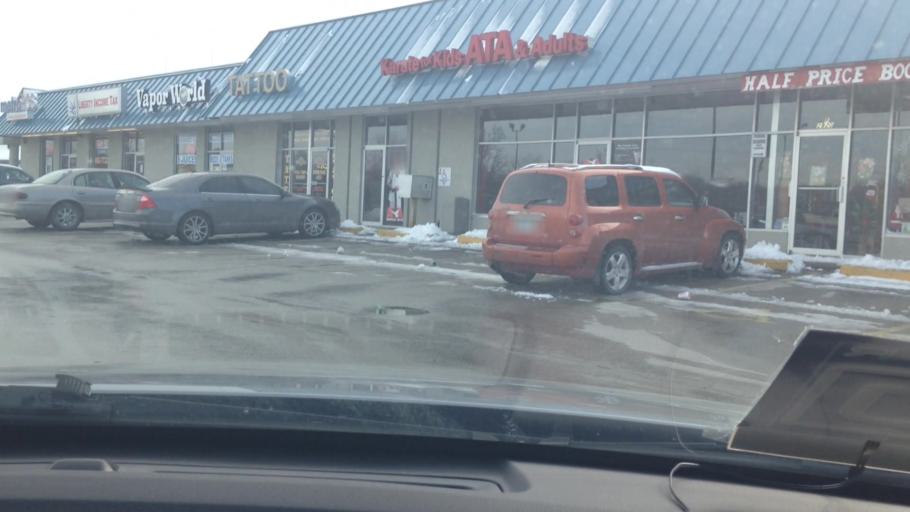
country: US
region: Kansas
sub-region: Leavenworth County
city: Leavenworth
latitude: 39.2874
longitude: -94.9070
